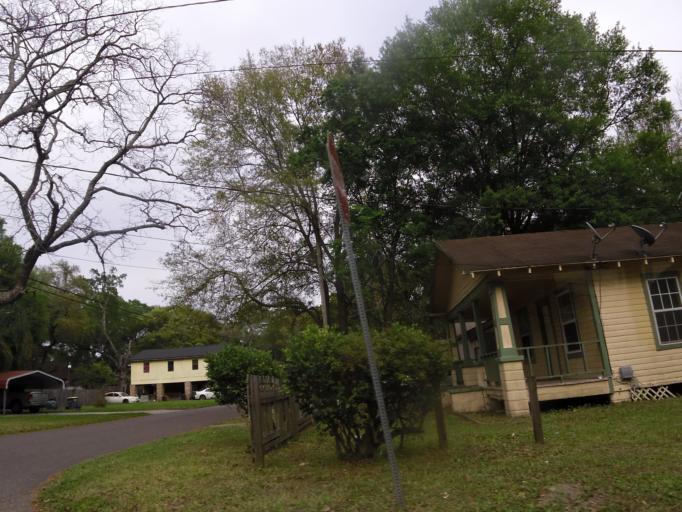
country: US
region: Florida
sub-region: Duval County
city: Jacksonville
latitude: 30.3260
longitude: -81.7118
